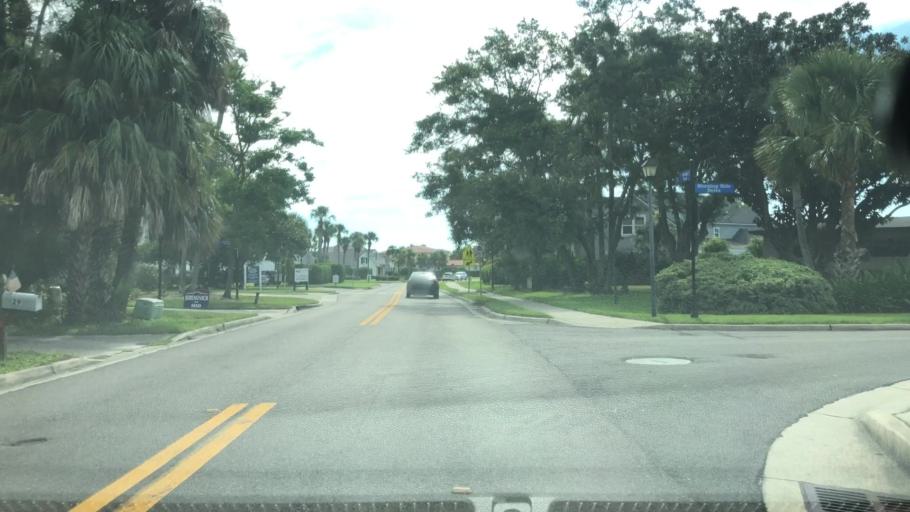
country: US
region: Florida
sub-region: Saint Johns County
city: Ponte Vedra Beach
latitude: 30.2274
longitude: -81.3818
